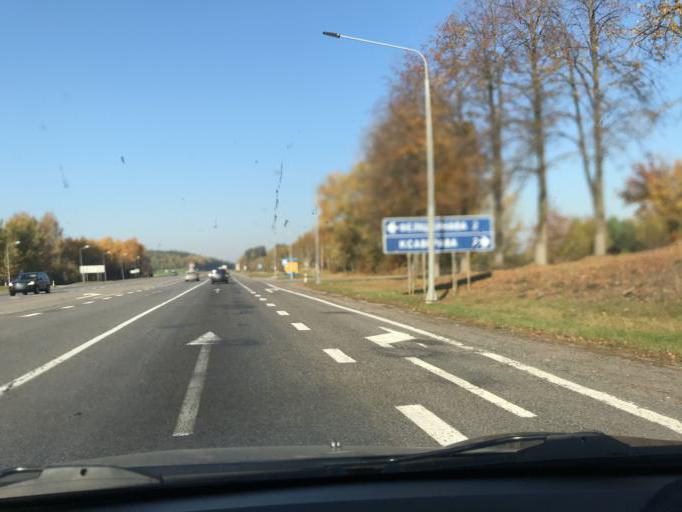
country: BY
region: Minsk
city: Luhavaya Slabada
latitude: 53.7571
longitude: 27.8307
